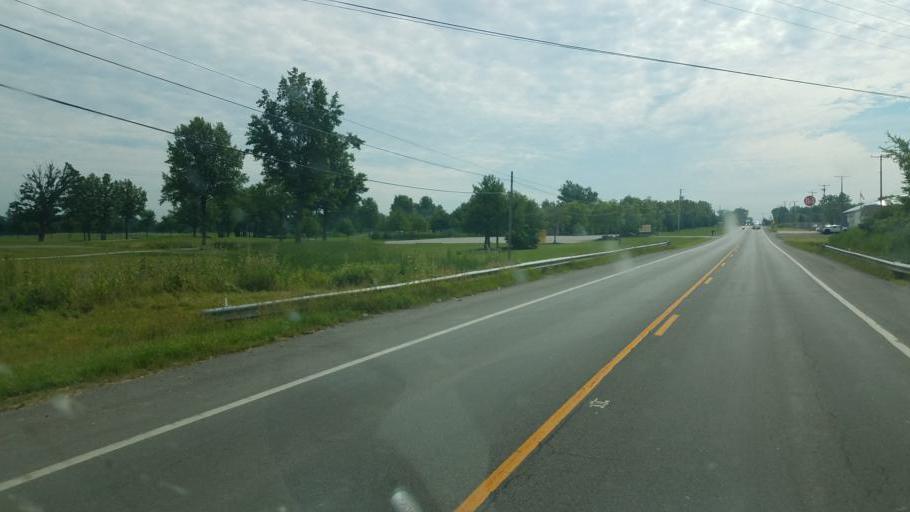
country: US
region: Ohio
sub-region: Lorain County
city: Eaton Estates
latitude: 41.3137
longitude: -81.9895
